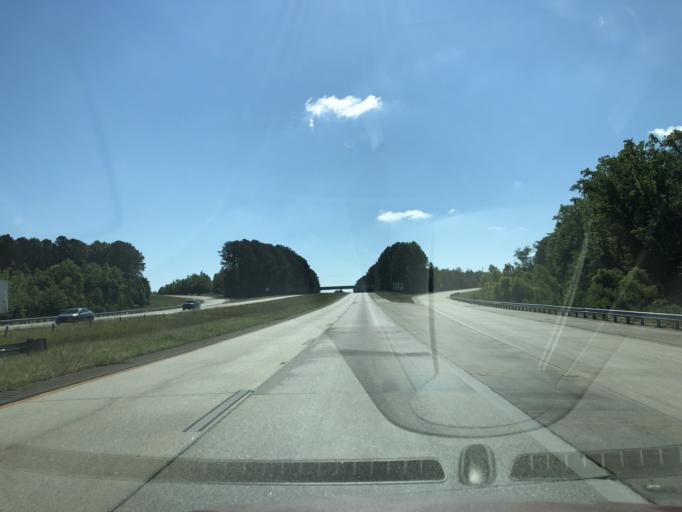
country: US
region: Georgia
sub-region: McDuffie County
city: Thomson
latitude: 33.5051
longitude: -82.5605
